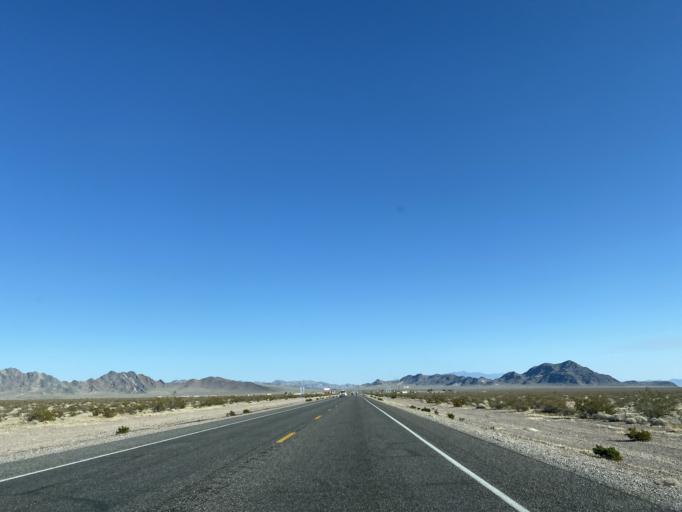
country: US
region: Nevada
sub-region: Nye County
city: Beatty
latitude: 36.6472
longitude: -116.4137
